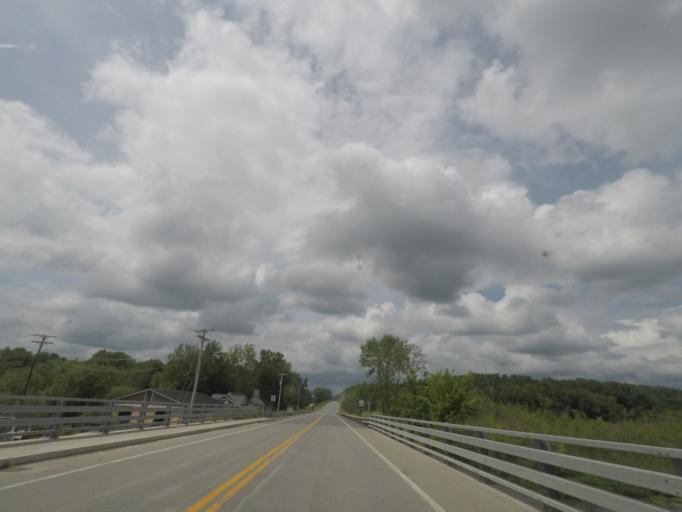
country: US
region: New York
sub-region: Saratoga County
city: Saratoga Springs
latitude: 43.0745
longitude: -73.6951
